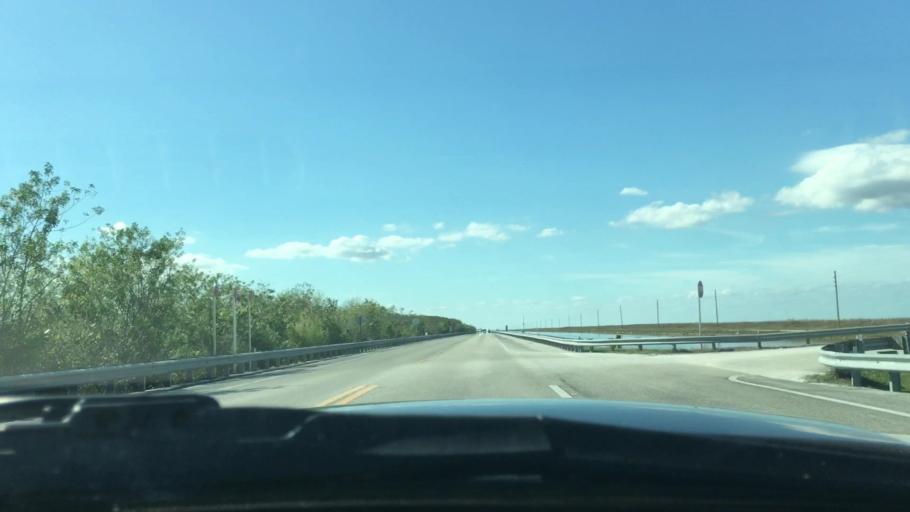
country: US
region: Florida
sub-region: Miami-Dade County
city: Kendall West
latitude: 25.7602
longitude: -80.5022
